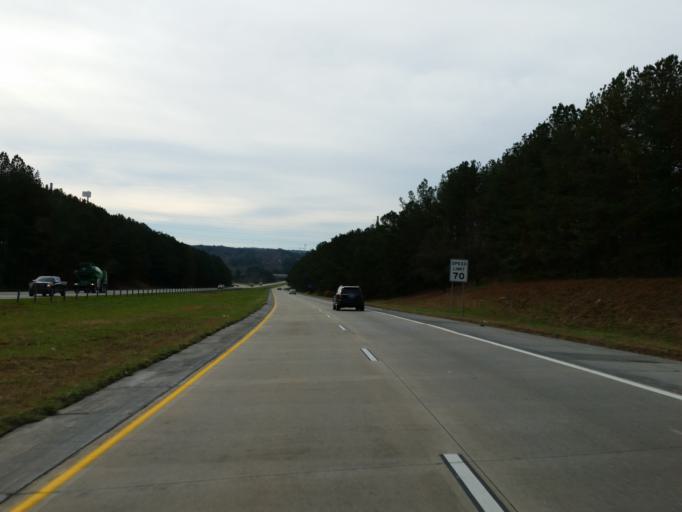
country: US
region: Georgia
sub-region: Cherokee County
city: Canton
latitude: 34.2661
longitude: -84.4678
